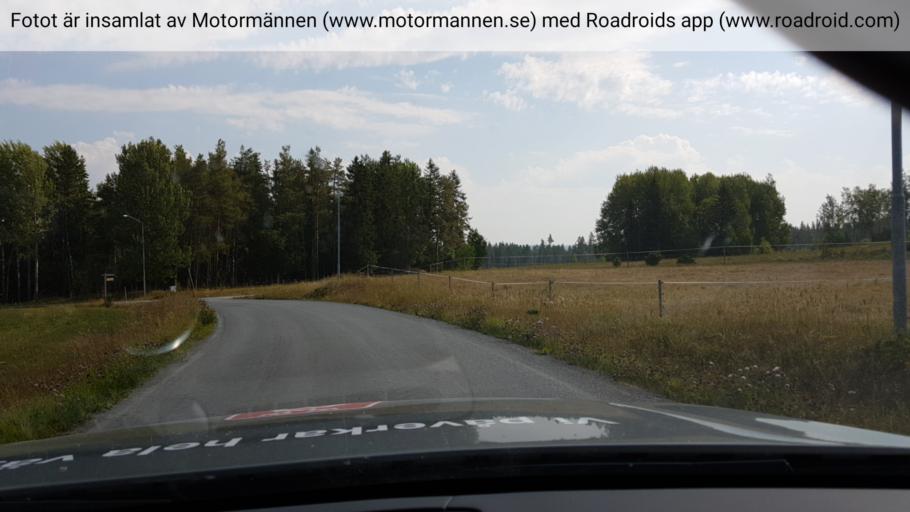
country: SE
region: Jaemtland
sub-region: OEstersunds Kommun
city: Ostersund
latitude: 63.1278
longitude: 14.6558
